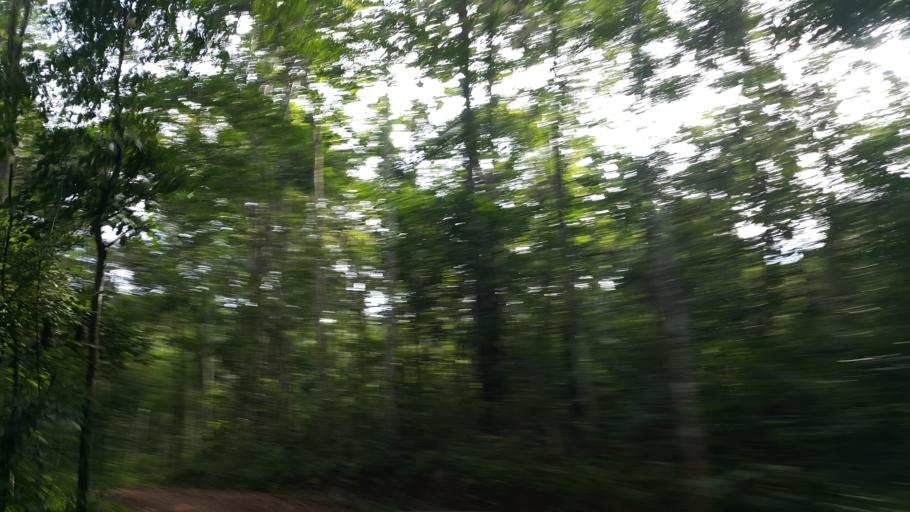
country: TH
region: Chiang Mai
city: Mae On
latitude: 18.8796
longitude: 99.2119
